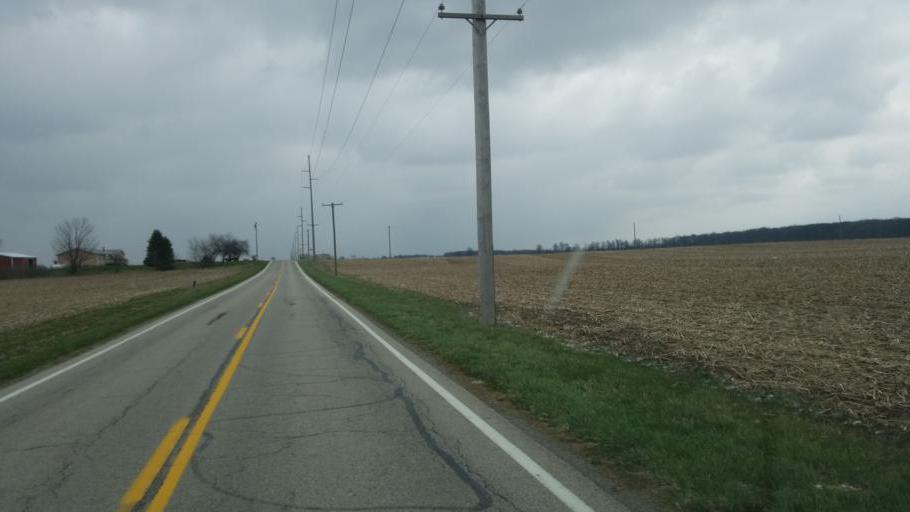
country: US
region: Ohio
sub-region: Union County
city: Richwood
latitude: 40.4514
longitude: -83.3687
